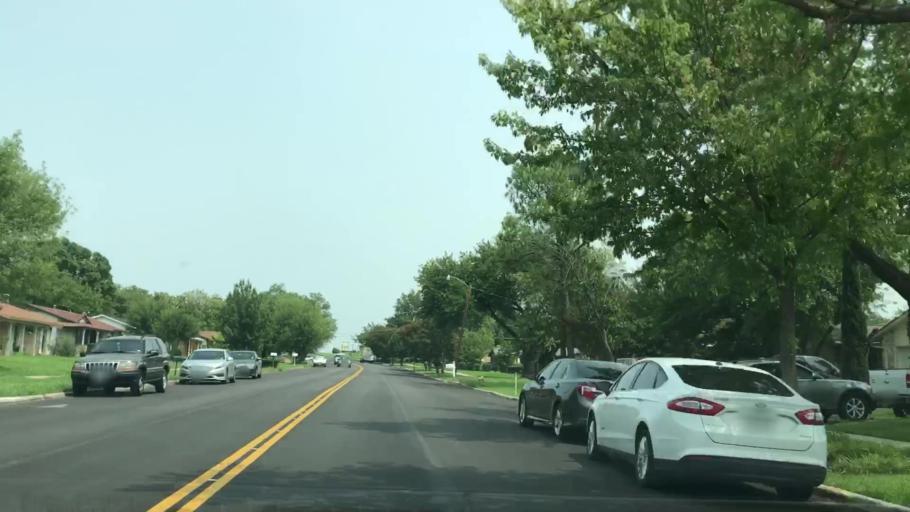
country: US
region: Texas
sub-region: Dallas County
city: Irving
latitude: 32.8475
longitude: -96.9986
